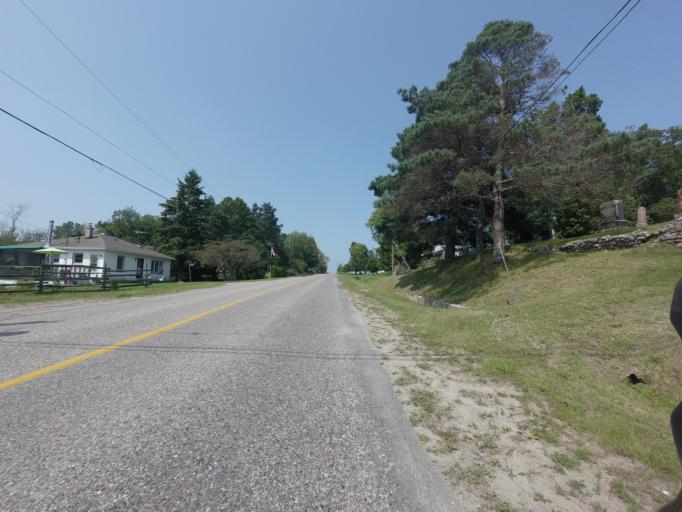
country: CA
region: Ontario
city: Skatepark
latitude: 44.6570
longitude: -76.7226
